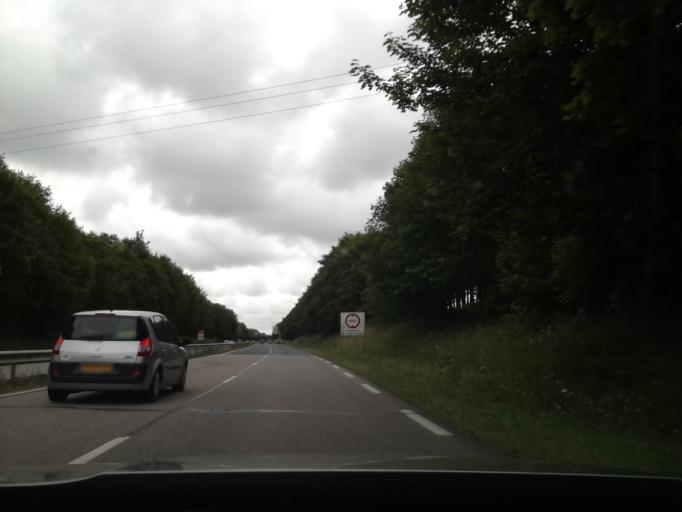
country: FR
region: Lower Normandy
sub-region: Departement du Calvados
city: Le Molay-Littry
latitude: 49.3322
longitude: -0.9098
